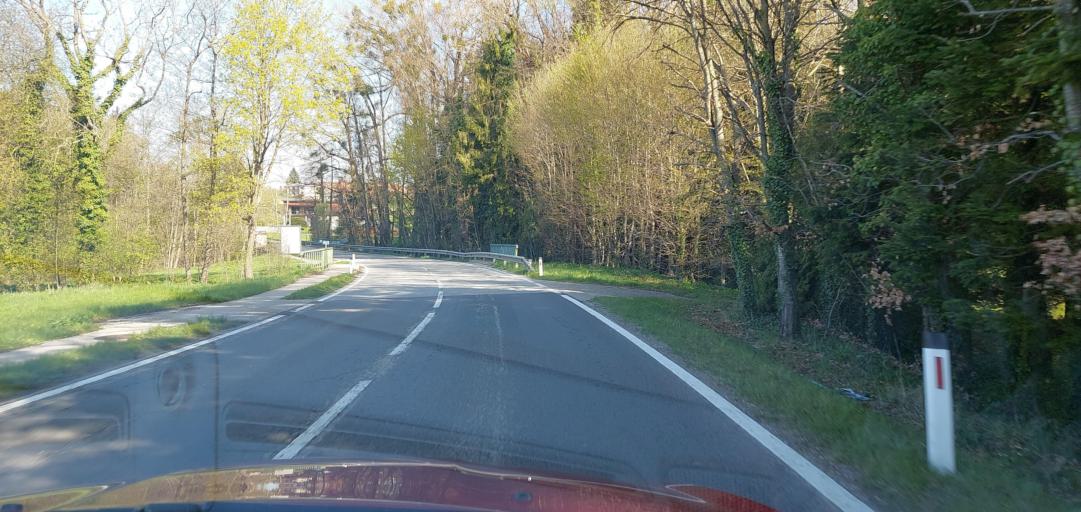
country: AT
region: Upper Austria
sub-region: Politischer Bezirk Ried im Innkreis
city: Ried im Innkreis
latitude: 48.1613
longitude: 13.5598
